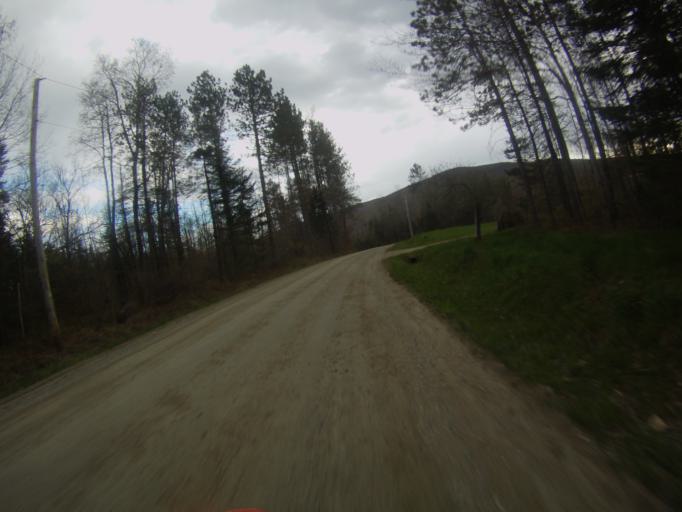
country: US
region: Vermont
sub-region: Addison County
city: Bristol
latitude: 44.0324
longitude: -73.0192
